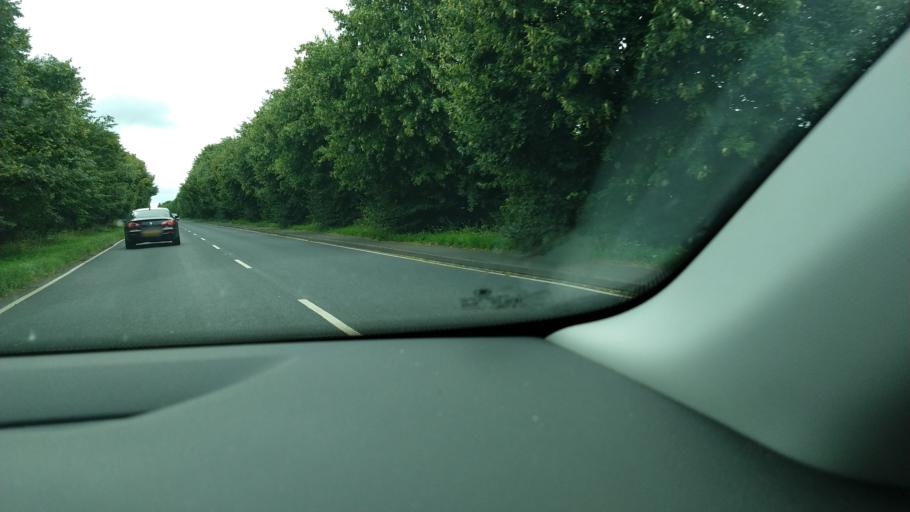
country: GB
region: England
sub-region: North Yorkshire
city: Camblesforth
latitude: 53.7263
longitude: -1.0091
